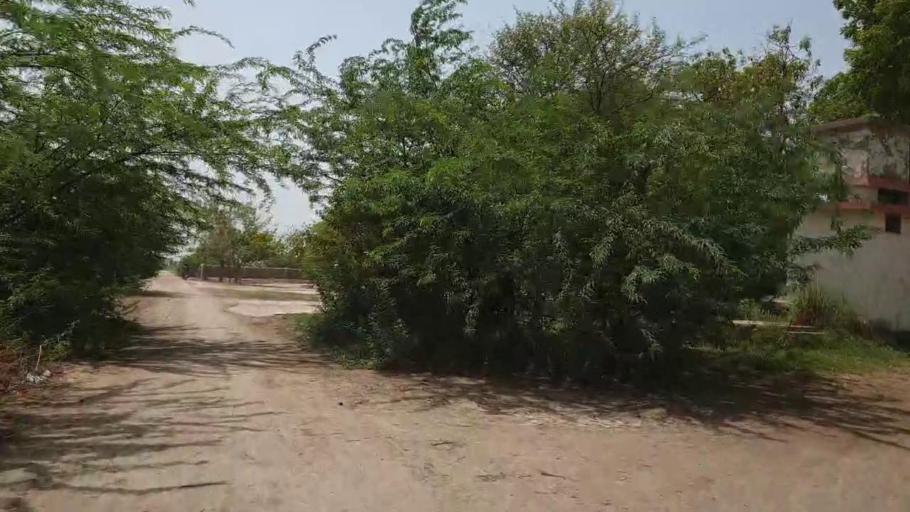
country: PK
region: Sindh
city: Daur
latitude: 26.3855
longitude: 68.4337
